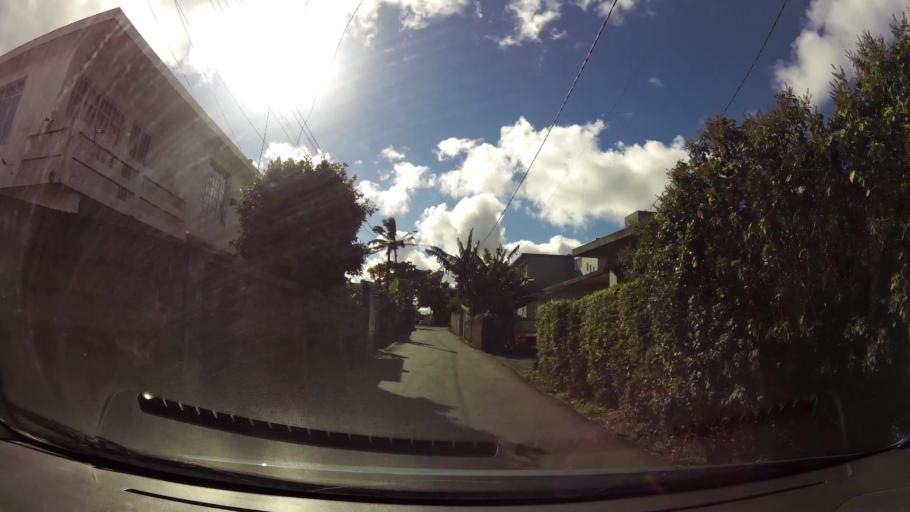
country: MU
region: Plaines Wilhems
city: Curepipe
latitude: -20.2982
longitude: 57.5173
